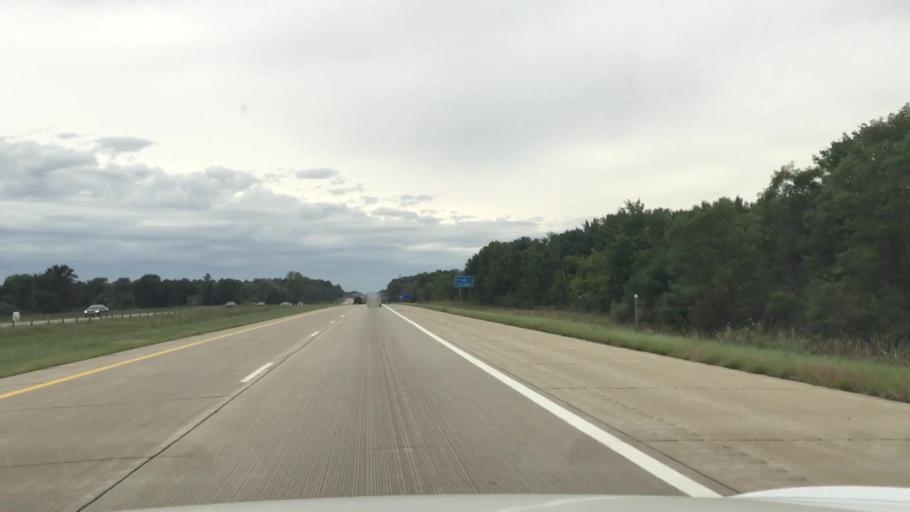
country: US
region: Michigan
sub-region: Saint Clair County
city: Marysville
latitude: 42.8750
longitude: -82.5400
